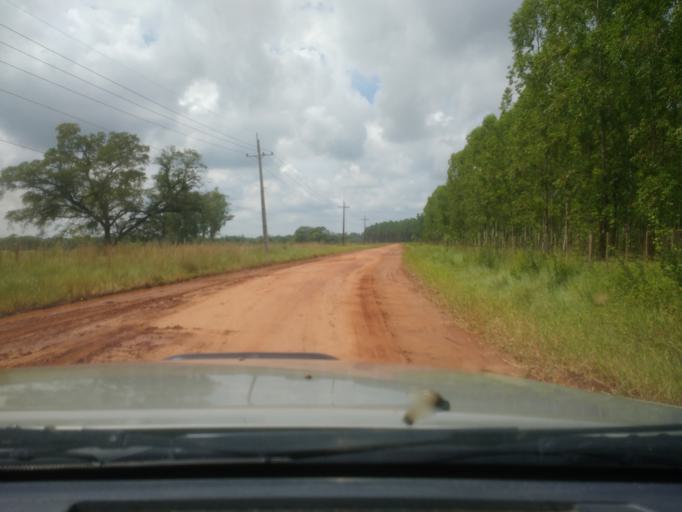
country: PY
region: San Pedro
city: Puerto Rosario
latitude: -24.3988
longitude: -57.1041
